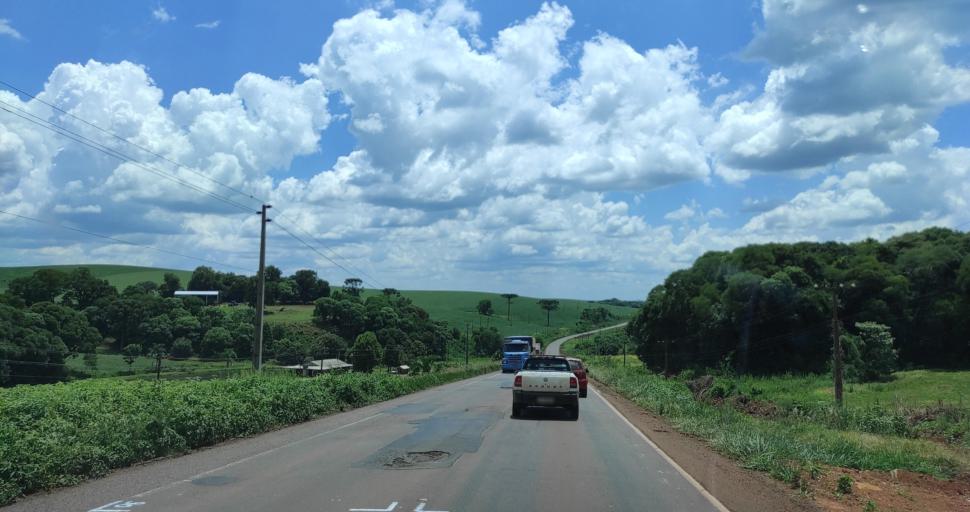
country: BR
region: Santa Catarina
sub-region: Xanxere
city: Xanxere
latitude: -26.8278
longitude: -52.4145
